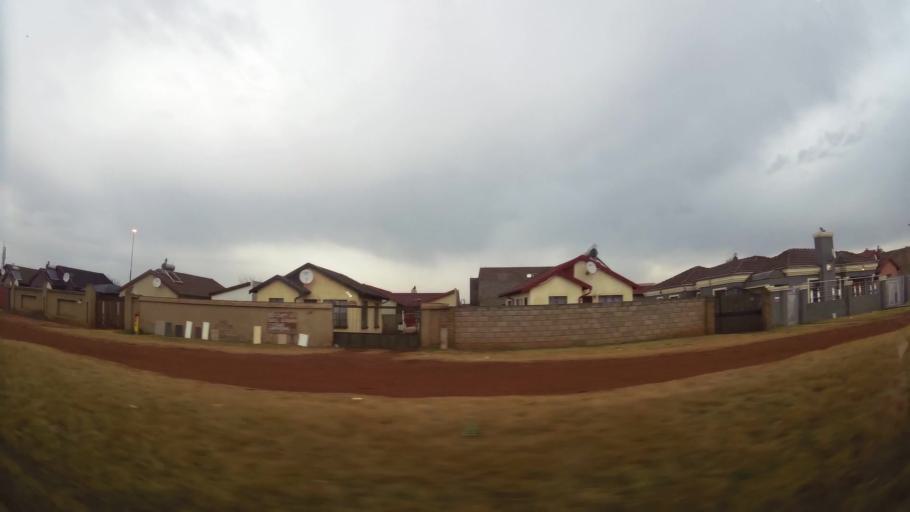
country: ZA
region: Gauteng
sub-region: Ekurhuleni Metropolitan Municipality
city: Germiston
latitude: -26.3297
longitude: 28.1977
